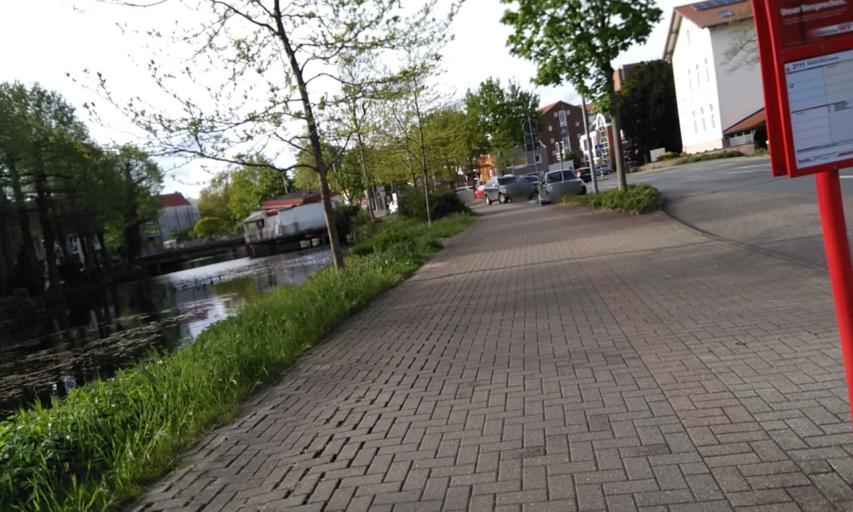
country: DE
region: Lower Saxony
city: Buxtehude
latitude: 53.4767
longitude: 9.7032
